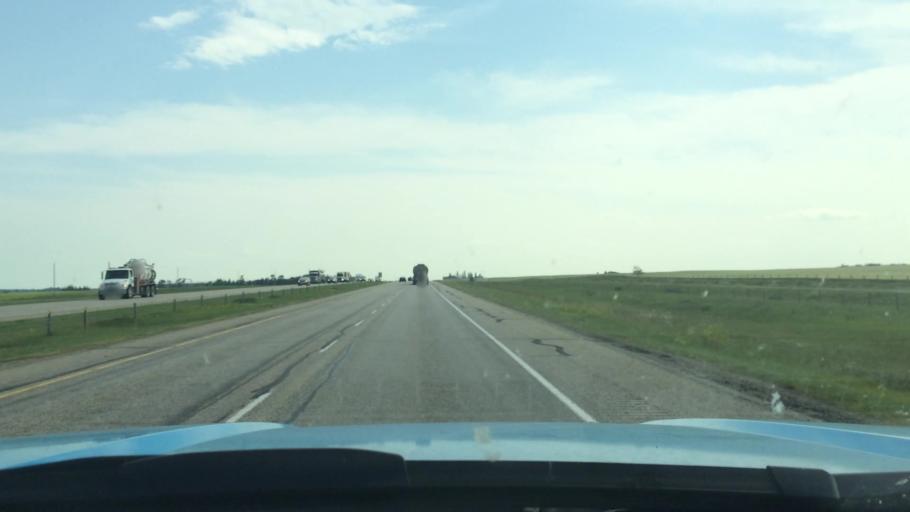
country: CA
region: Alberta
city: Olds
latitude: 51.8243
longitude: -114.0256
